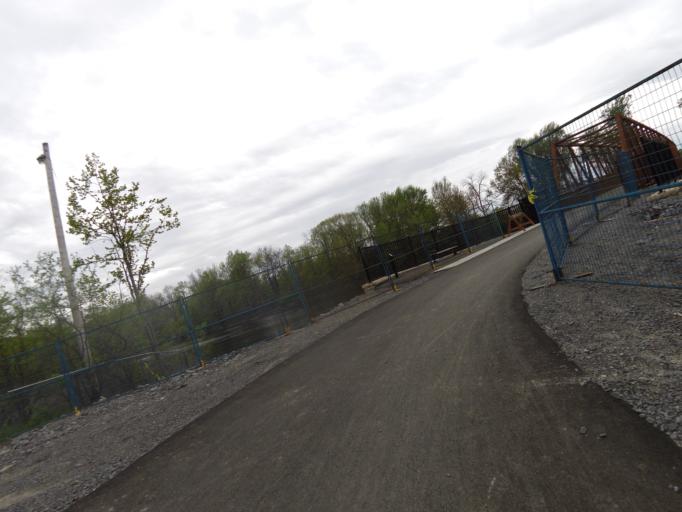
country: CA
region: Quebec
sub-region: Outaouais
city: Gatineau
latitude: 45.4500
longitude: -75.7069
